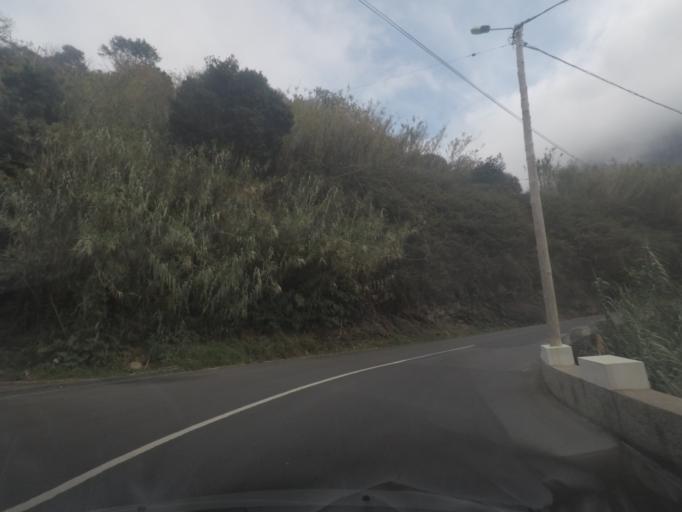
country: PT
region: Madeira
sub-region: Camara de Lobos
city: Curral das Freiras
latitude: 32.7330
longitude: -17.0272
